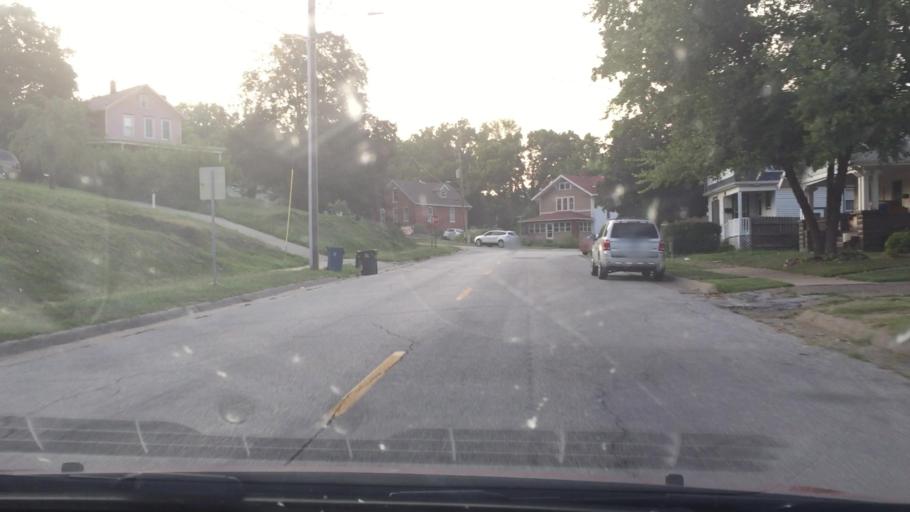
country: US
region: Iowa
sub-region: Muscatine County
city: Muscatine
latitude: 41.4297
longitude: -91.0540
